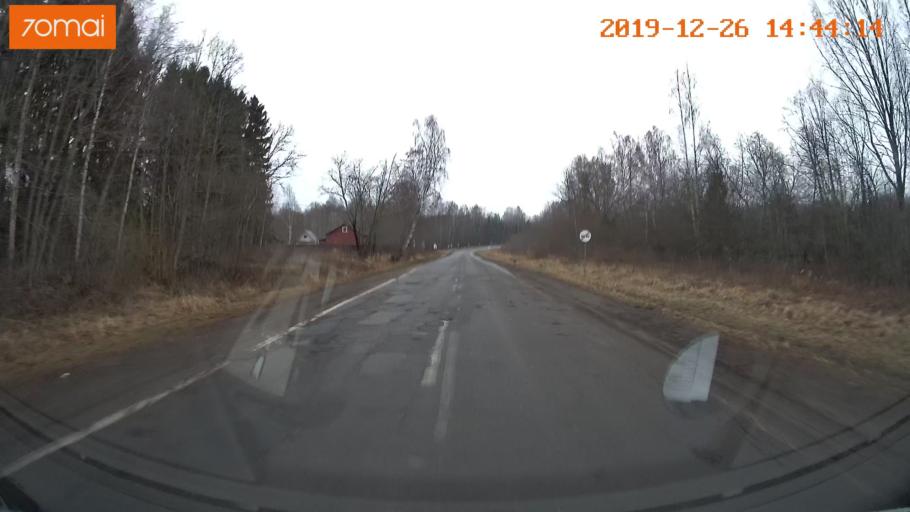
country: RU
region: Jaroslavl
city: Poshekhon'ye
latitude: 58.3500
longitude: 39.0485
